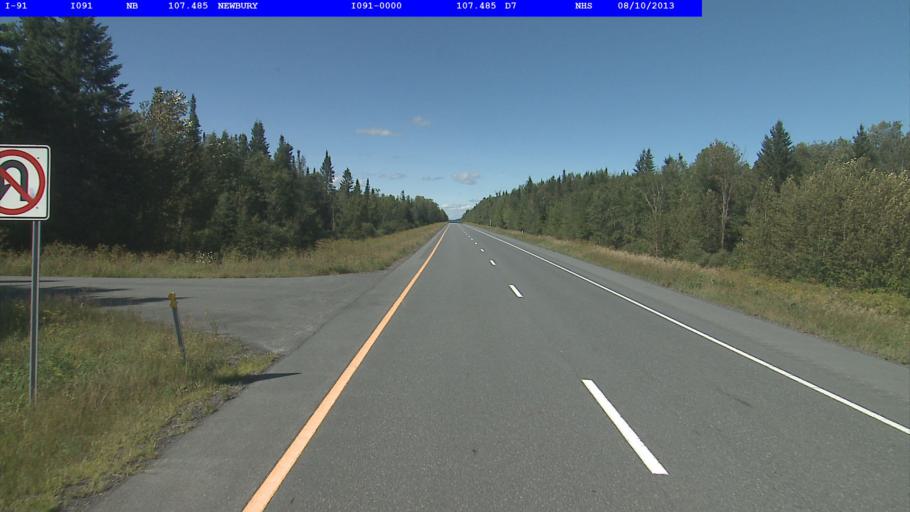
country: US
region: New Hampshire
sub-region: Grafton County
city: Woodsville
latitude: 44.1209
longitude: -72.1048
